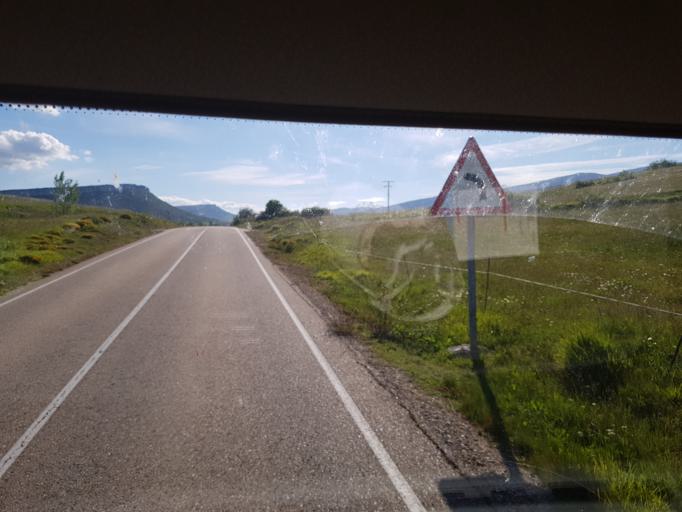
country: ES
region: Castille and Leon
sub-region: Provincia de Burgos
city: Espinosa de los Monteros
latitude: 43.0577
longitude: -3.6060
